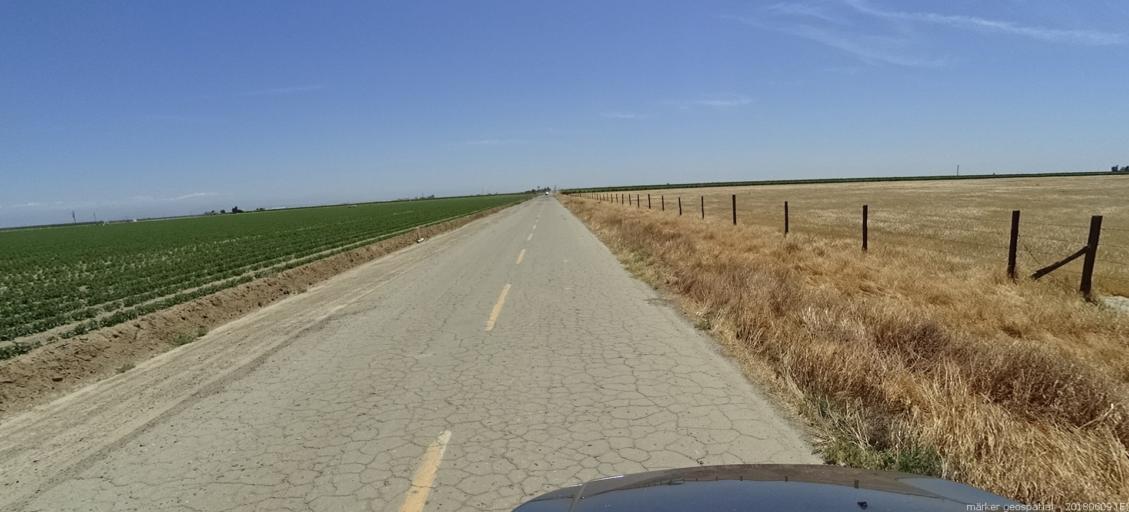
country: US
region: California
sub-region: Madera County
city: Fairmead
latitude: 36.9383
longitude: -120.2774
